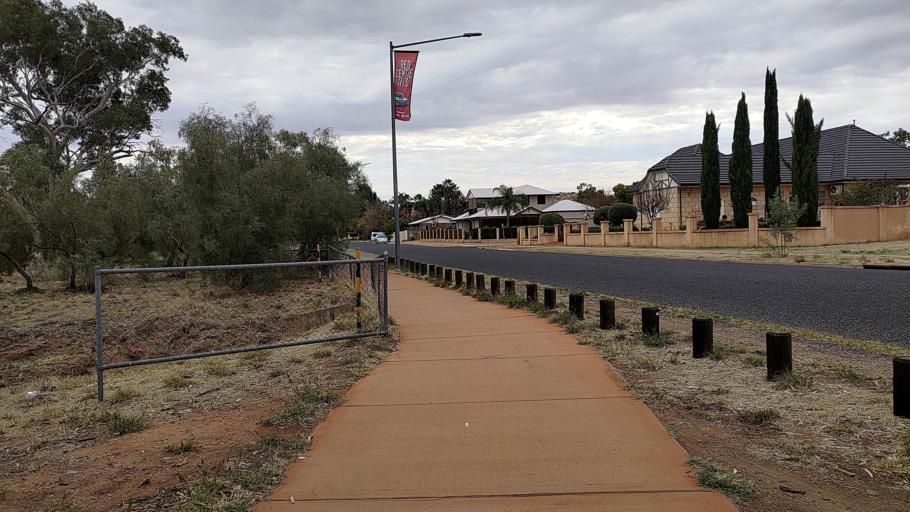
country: AU
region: Northern Territory
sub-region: Alice Springs
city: Alice Springs
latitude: -23.7111
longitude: 133.8803
